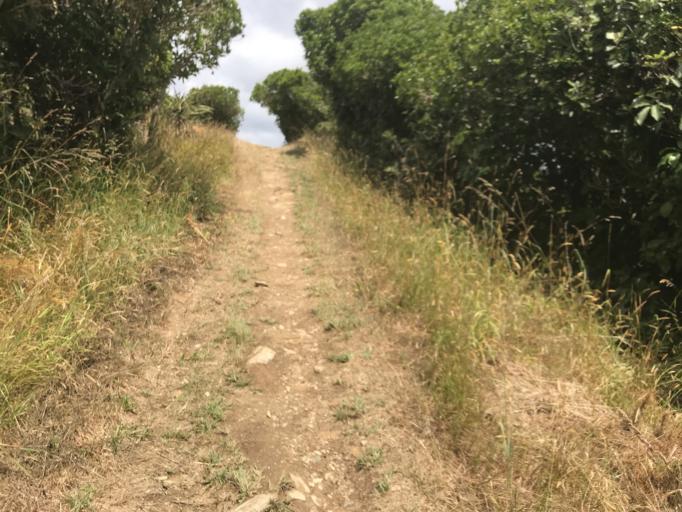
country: NZ
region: Marlborough
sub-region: Marlborough District
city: Picton
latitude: -41.2116
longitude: 174.0126
